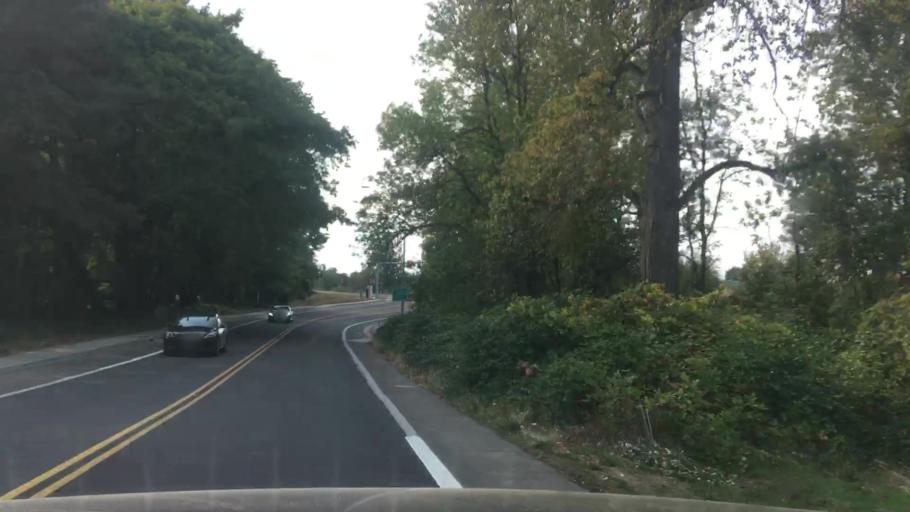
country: US
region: Oregon
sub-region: Lane County
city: Eugene
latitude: 44.0842
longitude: -123.0992
